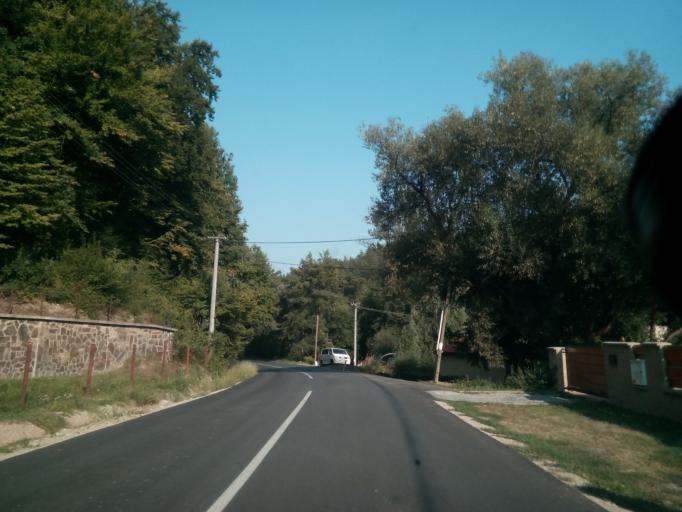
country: SK
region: Kosicky
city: Kosice
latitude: 48.7236
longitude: 21.1696
